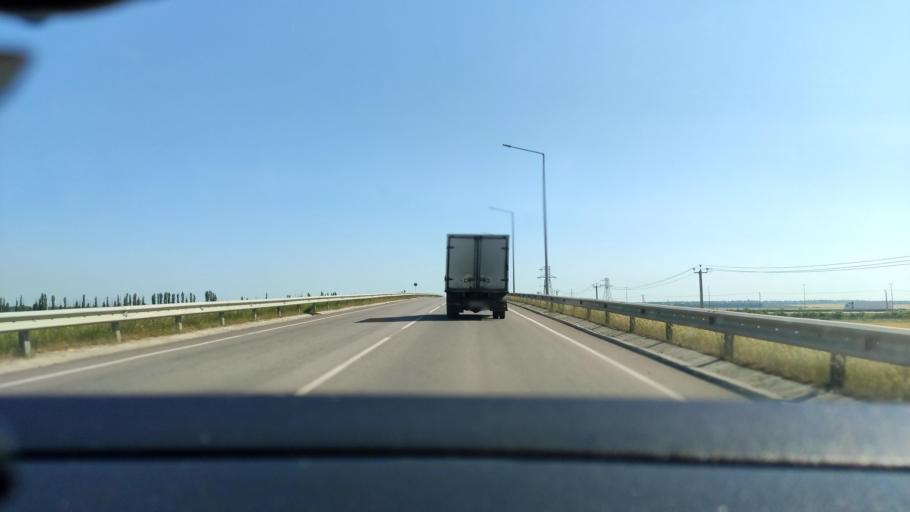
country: RU
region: Voronezj
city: Novaya Usman'
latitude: 51.5934
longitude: 39.3738
